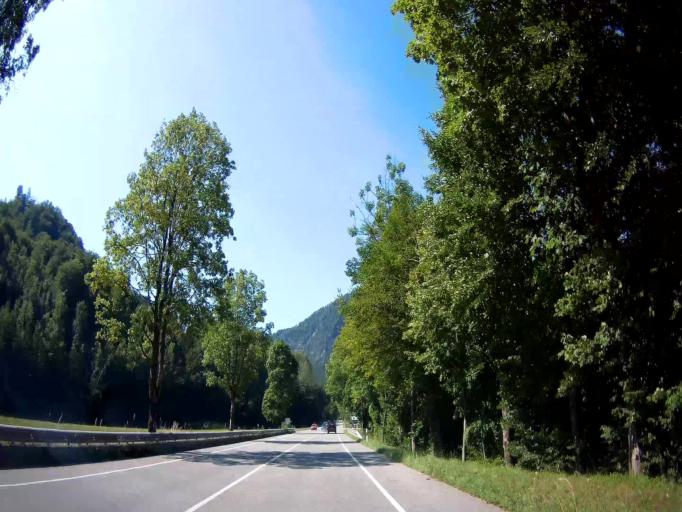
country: DE
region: Bavaria
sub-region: Upper Bavaria
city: Marktschellenberg
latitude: 47.6730
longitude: 13.0369
